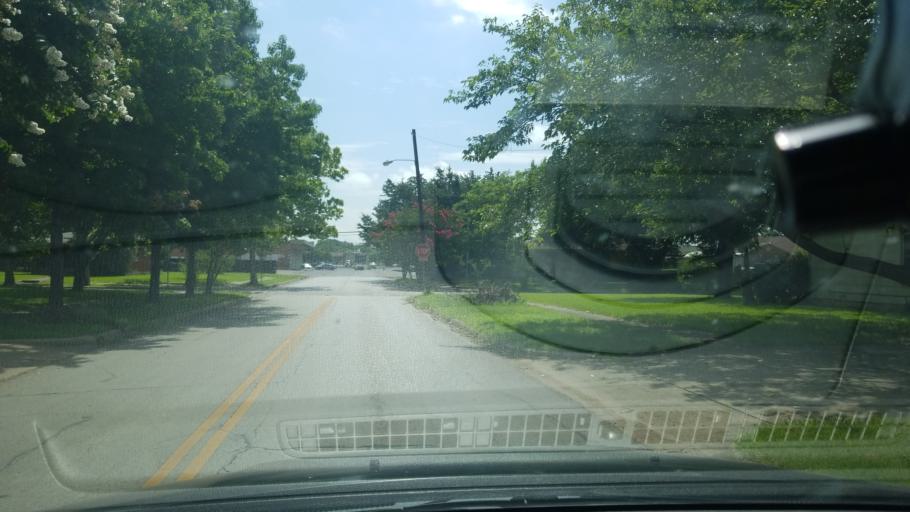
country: US
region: Texas
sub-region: Dallas County
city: Balch Springs
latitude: 32.7389
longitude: -96.6868
